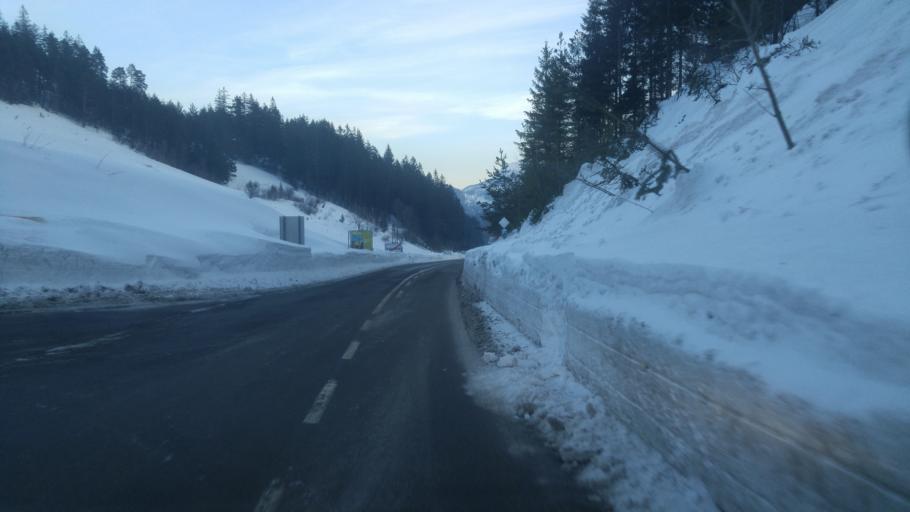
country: AT
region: Lower Austria
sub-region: Politischer Bezirk Wiener Neustadt
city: Rohr im Gebirge
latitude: 47.8870
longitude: 15.6839
